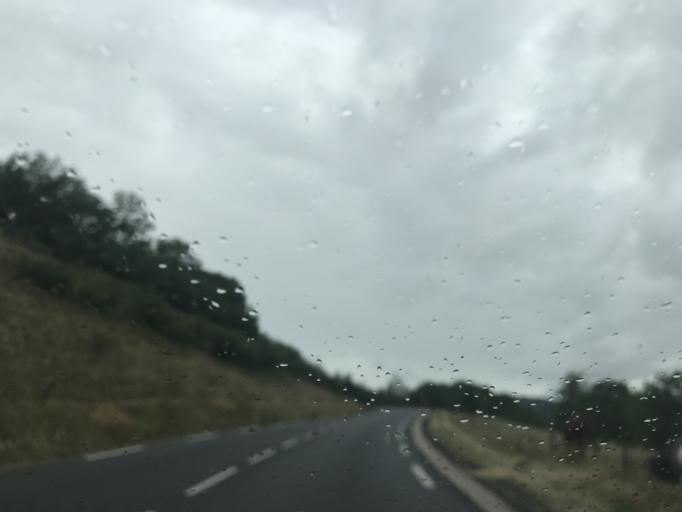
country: FR
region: Auvergne
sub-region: Departement de la Haute-Loire
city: Polignac
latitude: 45.0615
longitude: 3.8605
